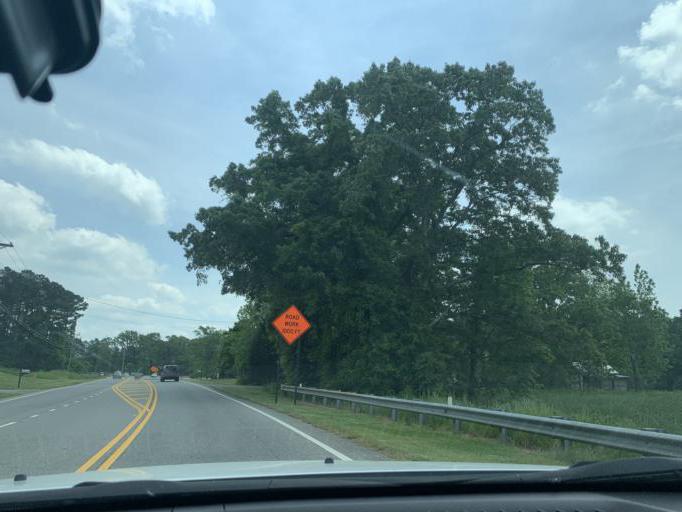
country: US
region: Georgia
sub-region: Forsyth County
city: Cumming
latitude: 34.1507
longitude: -84.1515
